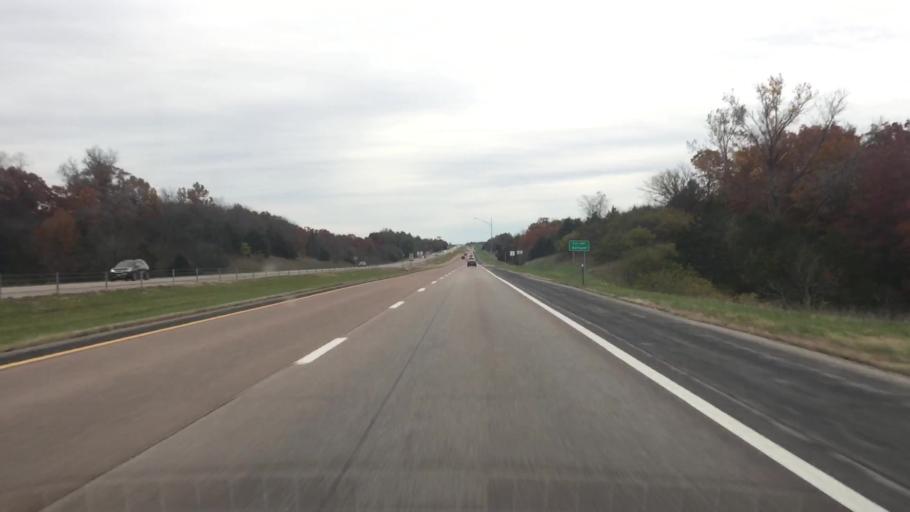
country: US
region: Missouri
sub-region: Boone County
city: Ashland
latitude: 38.7479
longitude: -92.2532
